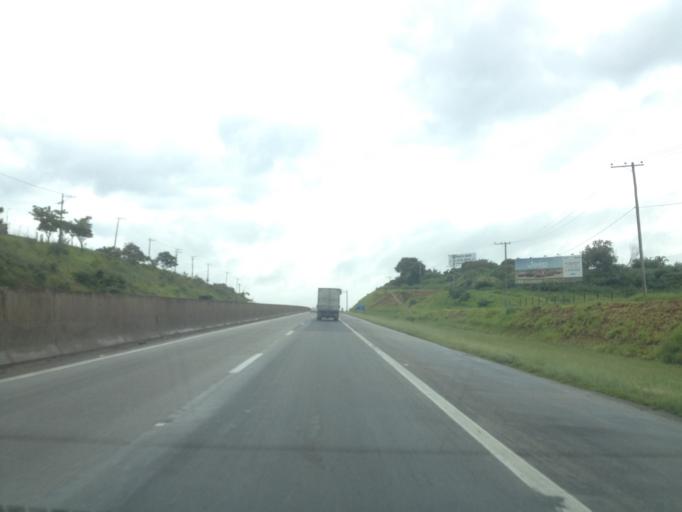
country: BR
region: Sao Paulo
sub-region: Itu
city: Itu
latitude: -23.2602
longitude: -47.3231
